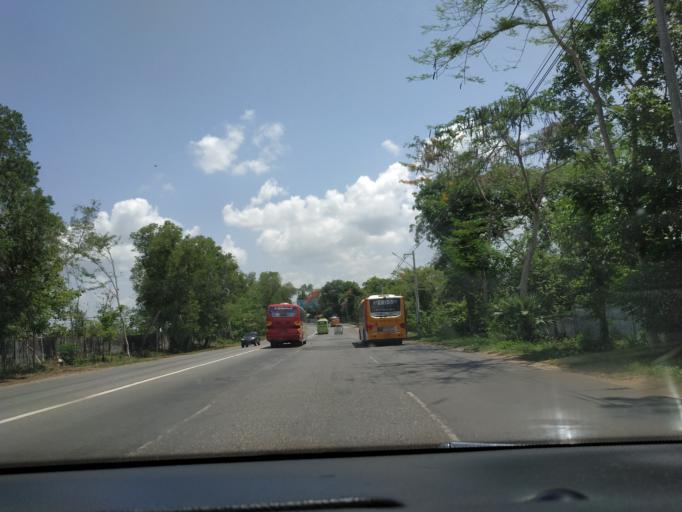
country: MM
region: Yangon
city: Yangon
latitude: 17.0032
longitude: 96.1293
